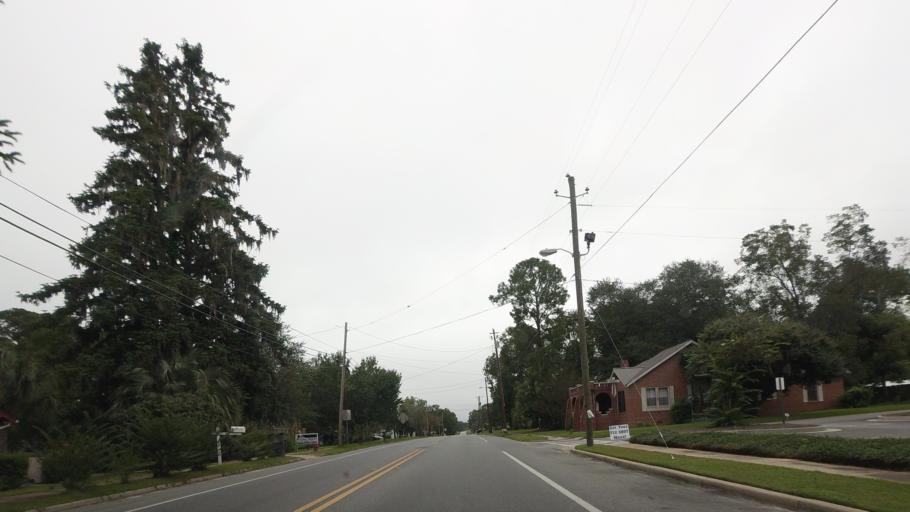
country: US
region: Georgia
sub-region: Berrien County
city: Nashville
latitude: 31.2103
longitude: -83.2498
